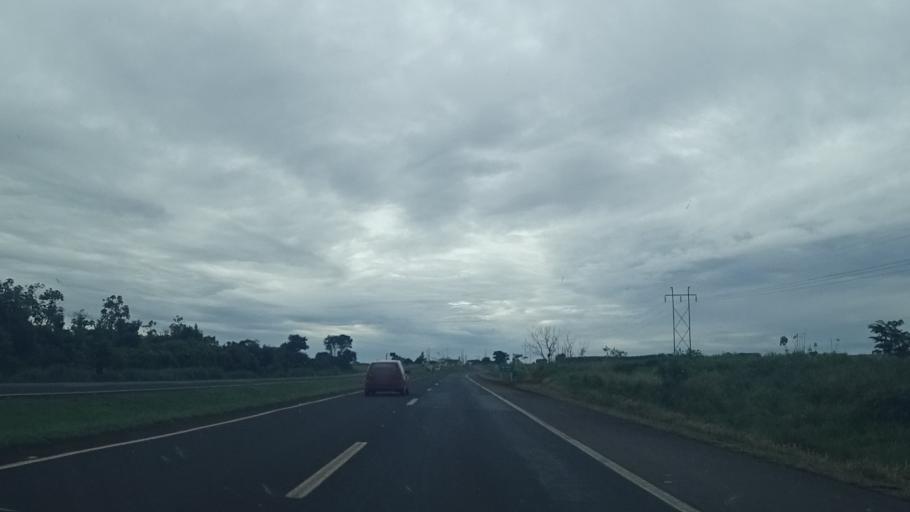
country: BR
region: Goias
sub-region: Itumbiara
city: Itumbiara
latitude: -18.2833
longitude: -49.2412
